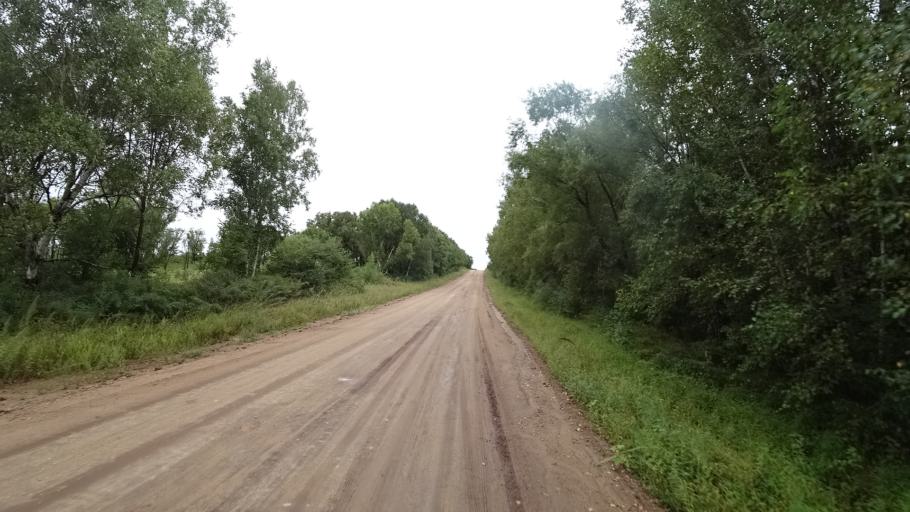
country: RU
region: Primorskiy
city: Ivanovka
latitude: 44.0423
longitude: 132.5408
